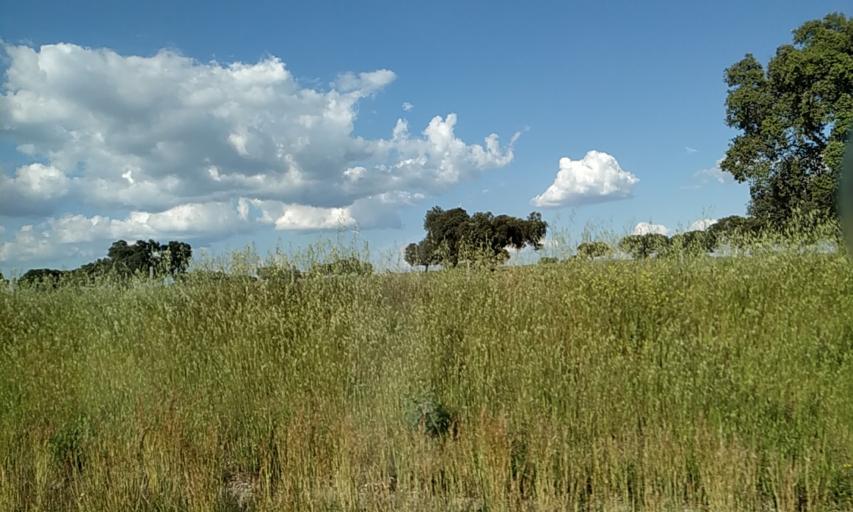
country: PT
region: Portalegre
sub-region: Portalegre
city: Urra
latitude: 39.1440
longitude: -7.4518
